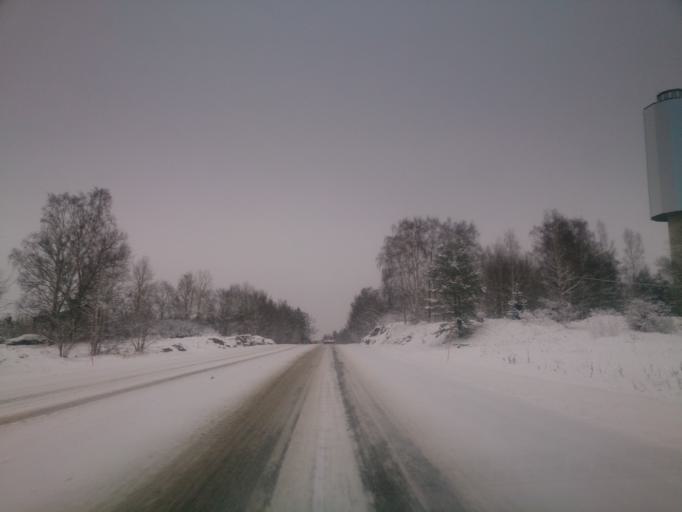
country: SE
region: OEstergoetland
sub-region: Norrkopings Kommun
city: Kimstad
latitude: 58.5012
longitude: 15.9732
